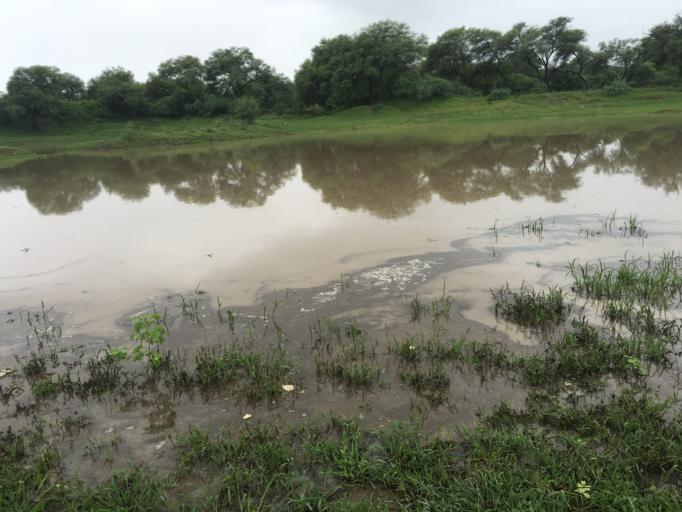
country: IN
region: Gujarat
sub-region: Mahesana
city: Kadi
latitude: 23.1619
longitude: 72.3788
